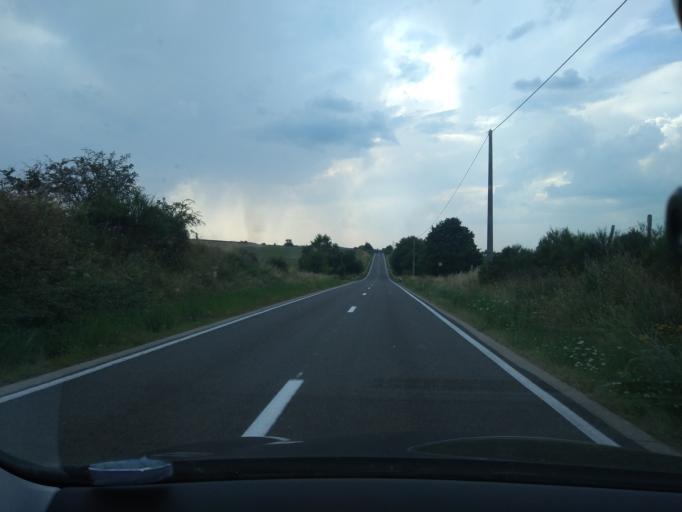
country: BE
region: Wallonia
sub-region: Province du Luxembourg
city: Bertogne
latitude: 50.0805
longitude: 5.6852
